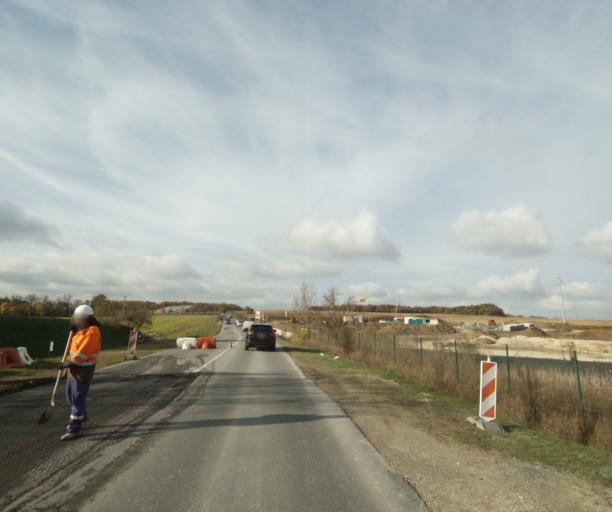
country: FR
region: Poitou-Charentes
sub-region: Departement de la Charente-Maritime
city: Saint-Georges-des-Coteaux
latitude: 45.7542
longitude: -0.6780
